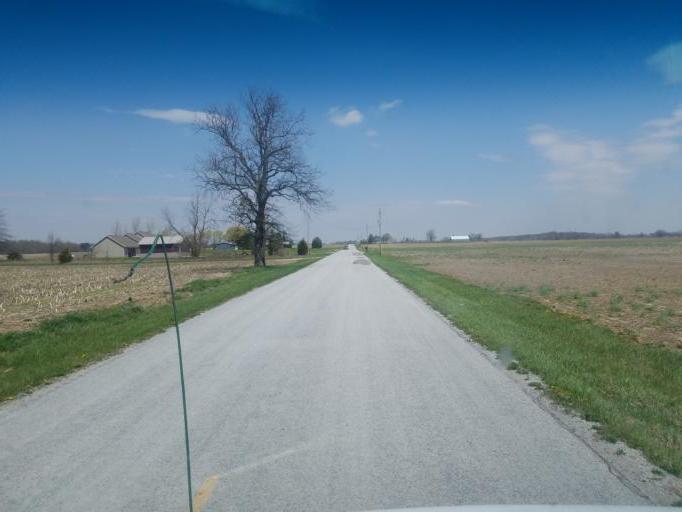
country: US
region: Ohio
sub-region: Hardin County
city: Kenton
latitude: 40.7100
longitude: -83.5379
